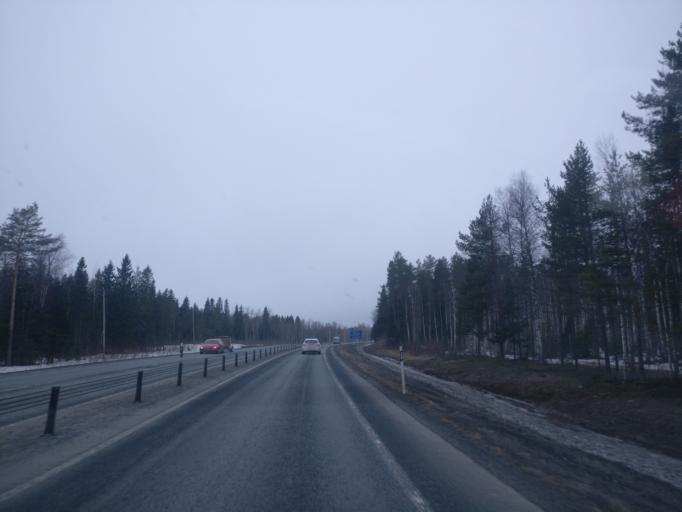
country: FI
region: Lapland
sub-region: Kemi-Tornio
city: Simo
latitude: 65.6686
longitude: 24.9375
